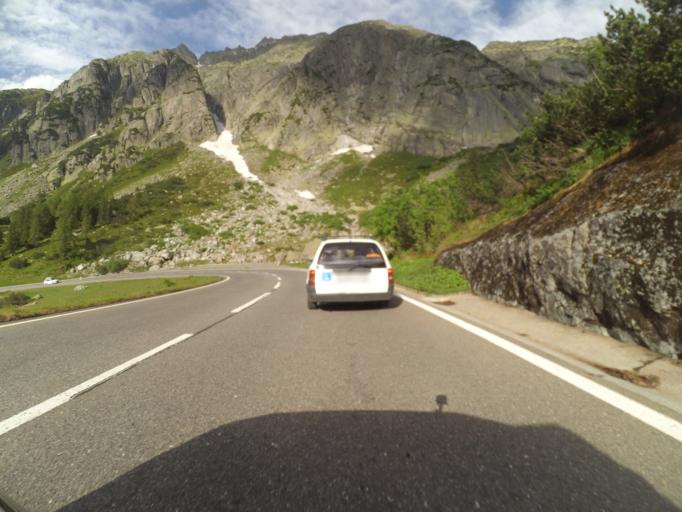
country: CH
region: Bern
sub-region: Interlaken-Oberhasli District
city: Meiringen
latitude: 46.5965
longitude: 8.3251
